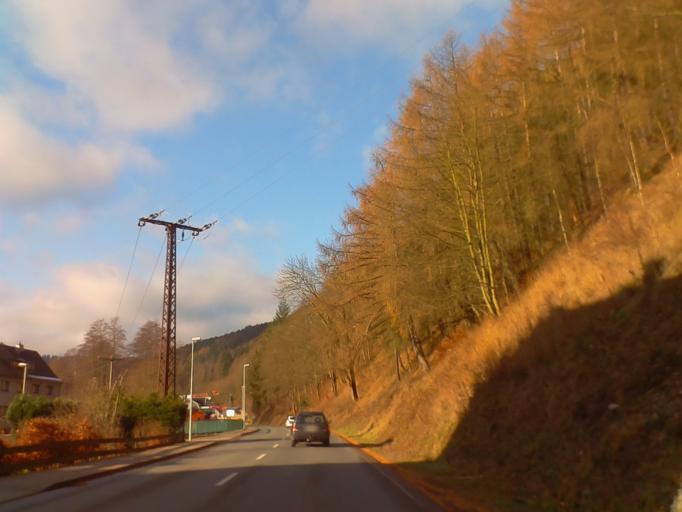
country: DE
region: Thuringia
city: Katzhutte
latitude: 50.5492
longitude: 11.0494
